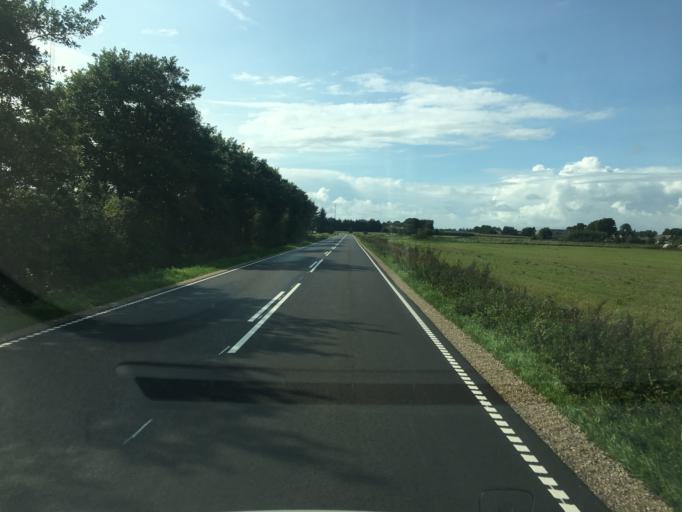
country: DK
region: South Denmark
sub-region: Tonder Kommune
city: Tonder
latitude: 55.0156
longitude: 8.8575
